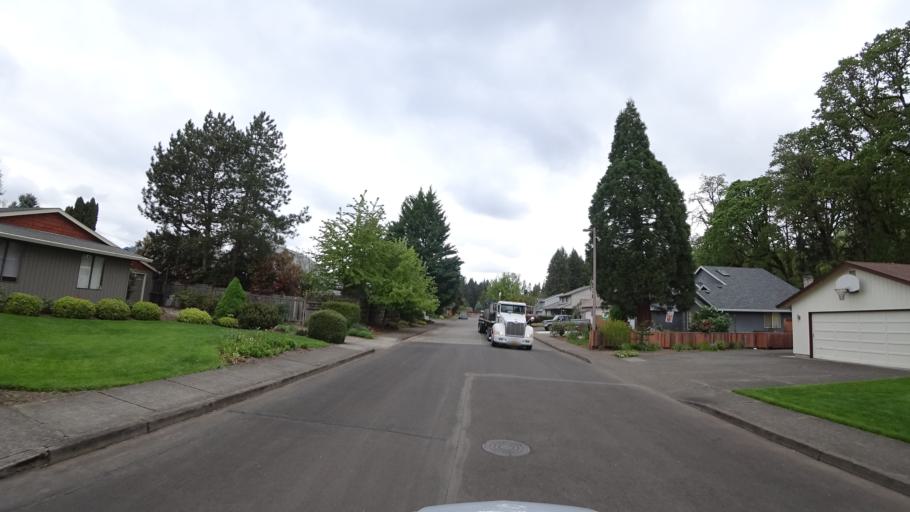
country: US
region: Oregon
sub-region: Washington County
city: Hillsboro
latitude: 45.5308
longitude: -122.9883
